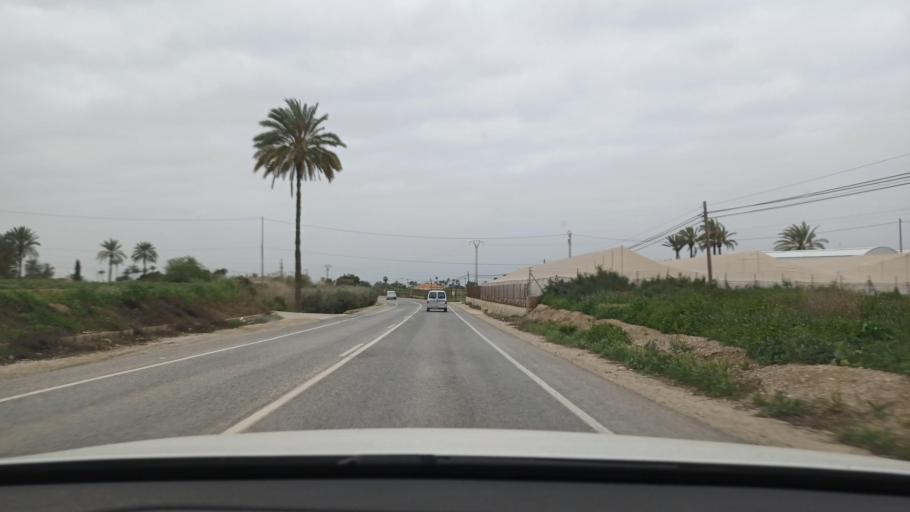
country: ES
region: Valencia
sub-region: Provincia de Alicante
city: Elche
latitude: 38.2374
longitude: -0.7131
